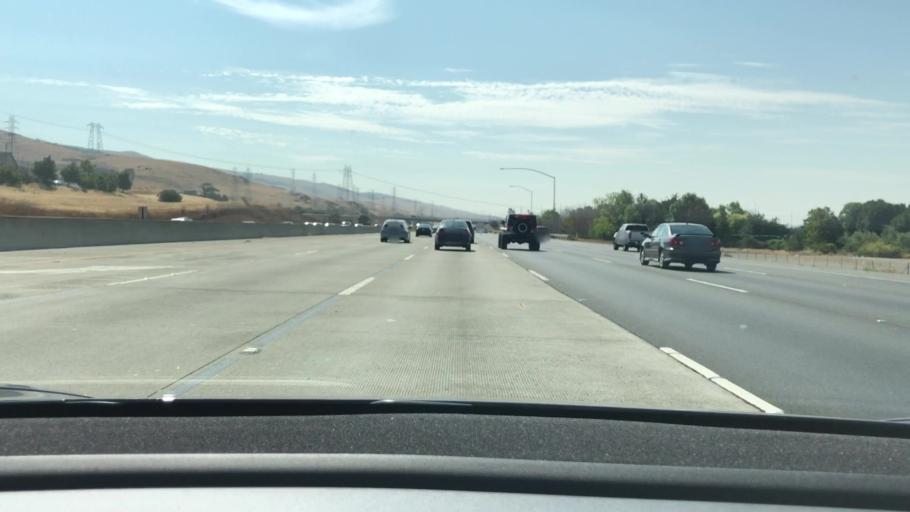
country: US
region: California
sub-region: Santa Clara County
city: Seven Trees
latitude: 37.2339
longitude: -121.7545
